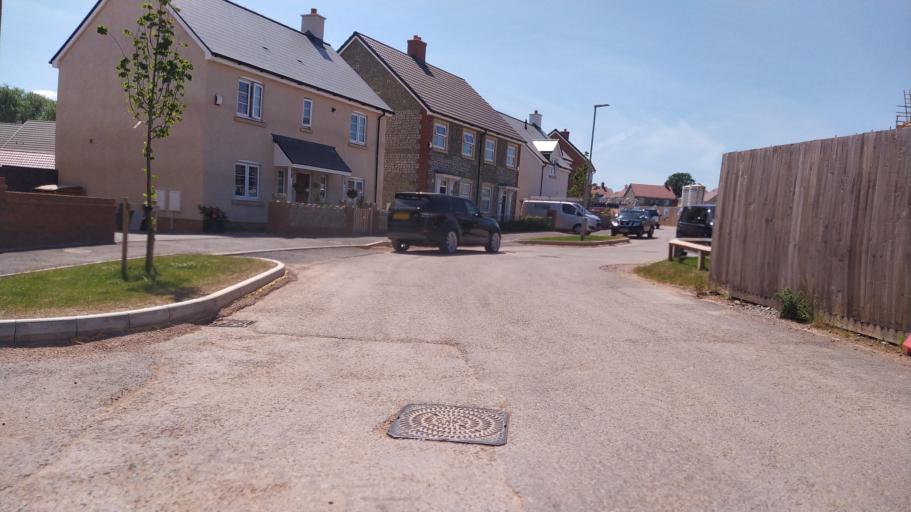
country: GB
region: England
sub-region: Somerset
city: Taunton
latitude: 51.0015
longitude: -3.0921
